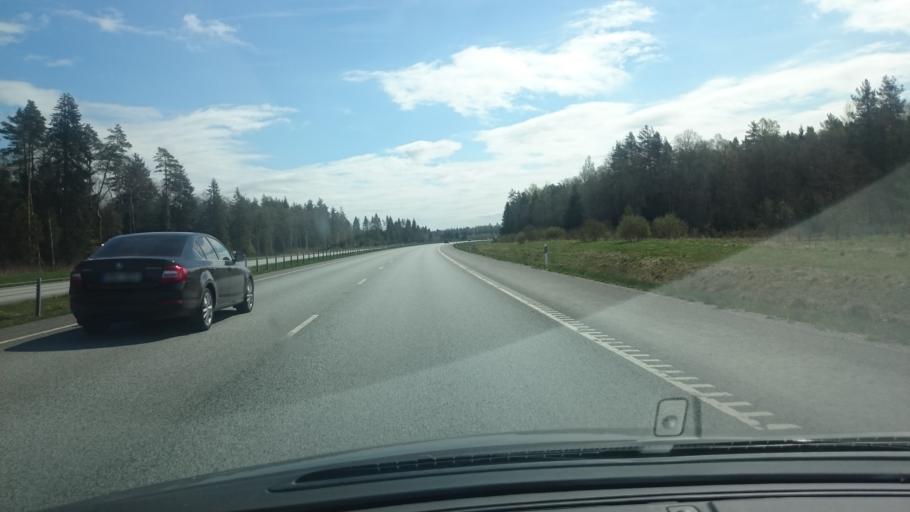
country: EE
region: Laeaene-Virumaa
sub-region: Kadrina vald
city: Kadrina
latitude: 59.4626
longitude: 26.0176
